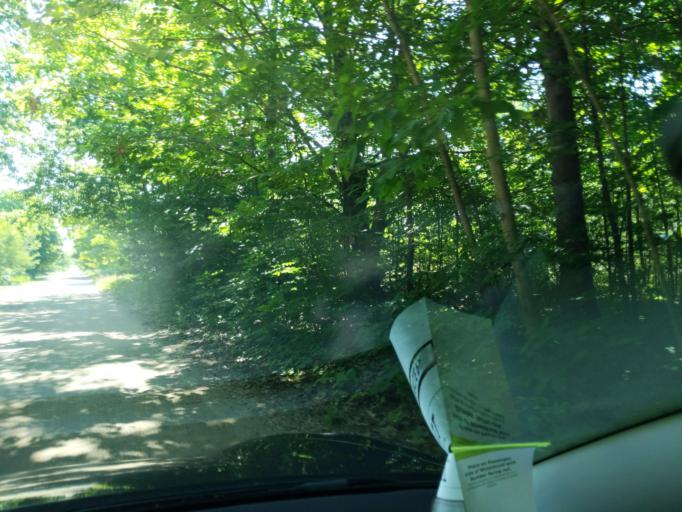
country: US
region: Michigan
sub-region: Mackinac County
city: Saint Ignace
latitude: 45.6983
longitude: -84.7271
